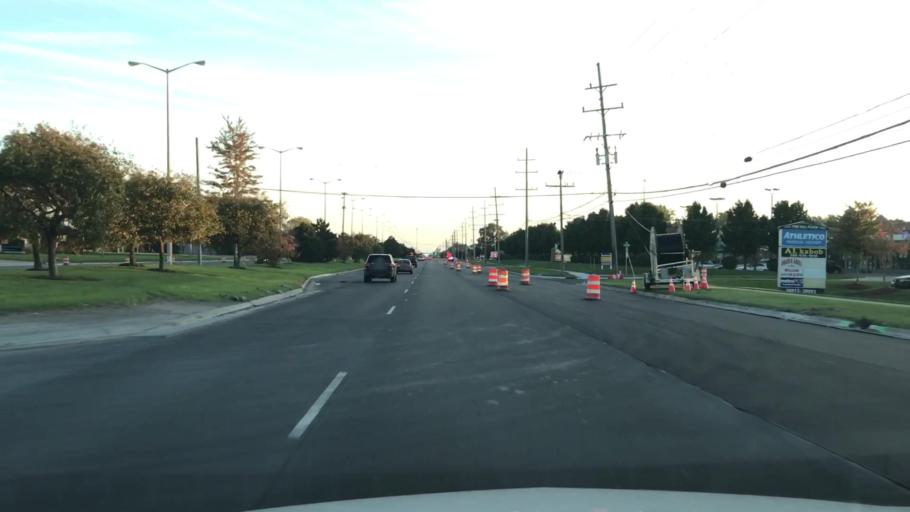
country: US
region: Michigan
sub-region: Macomb County
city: Sterling Heights
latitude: 42.5749
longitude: -83.0499
